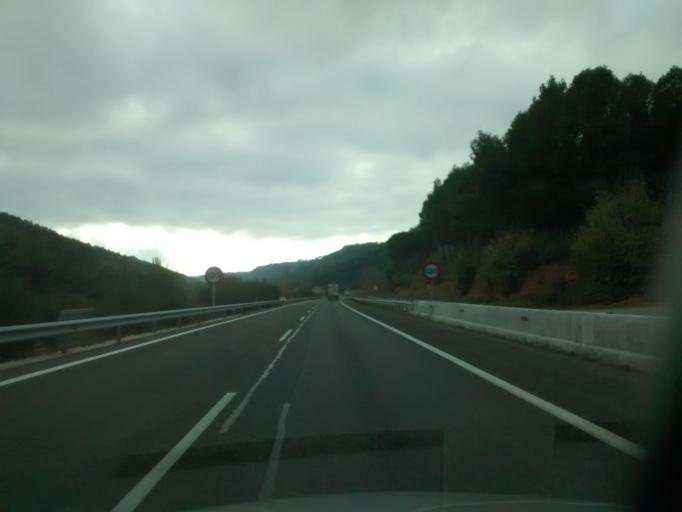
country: ES
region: Castille-La Mancha
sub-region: Provincia de Guadalajara
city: Torija
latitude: 40.7285
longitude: -3.0488
